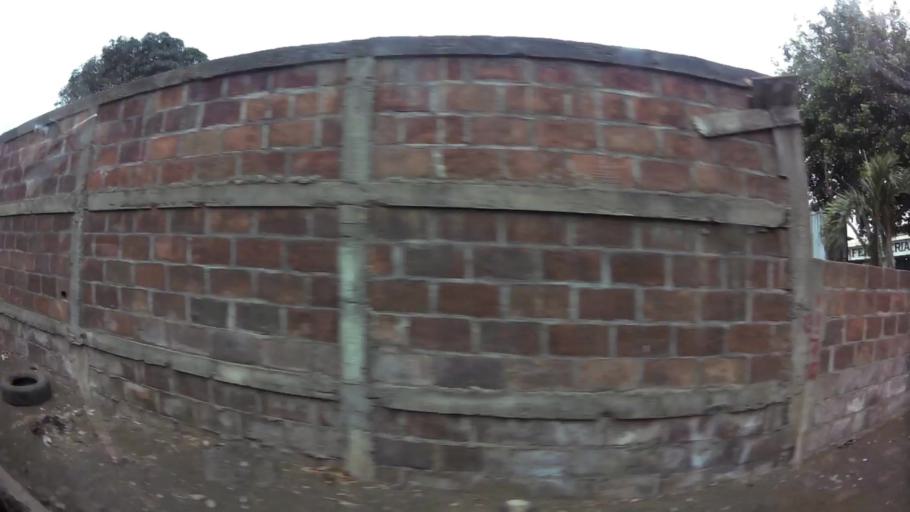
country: NI
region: Leon
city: Leon
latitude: 12.4509
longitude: -86.8639
